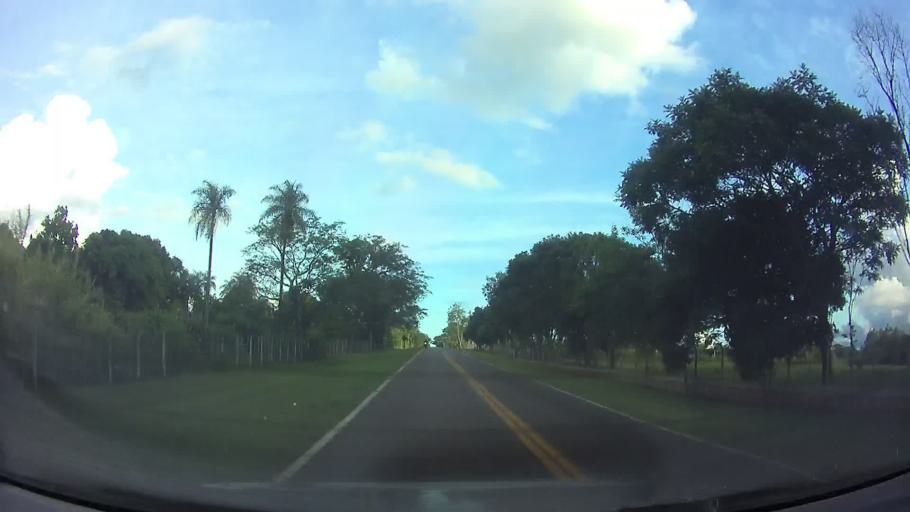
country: PY
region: Paraguari
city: Acahay
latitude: -25.9355
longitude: -57.1039
